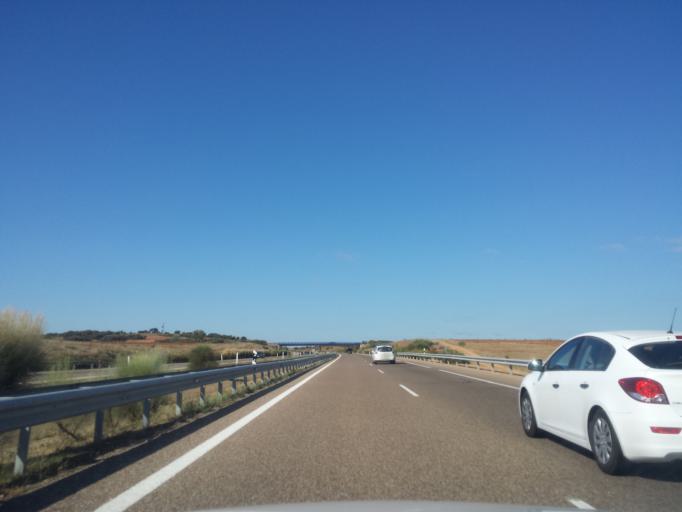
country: ES
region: Castille and Leon
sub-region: Provincia de Leon
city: Villamandos
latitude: 42.1891
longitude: -5.6159
